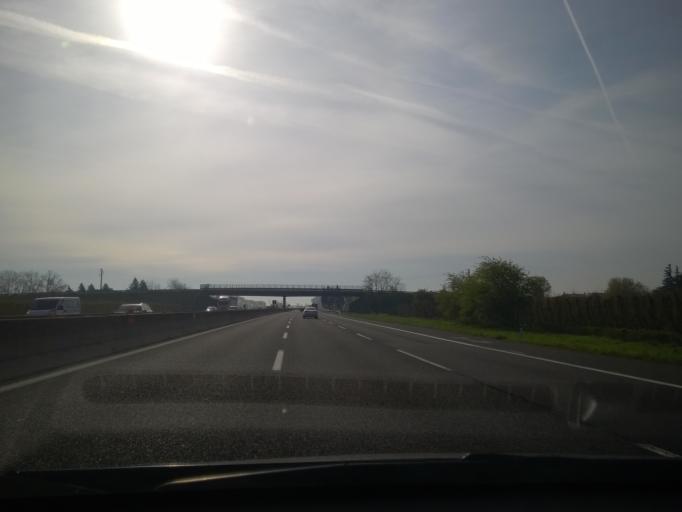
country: IT
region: Emilia-Romagna
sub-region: Provincia di Bologna
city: Mordano
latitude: 44.3681
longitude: 11.7766
